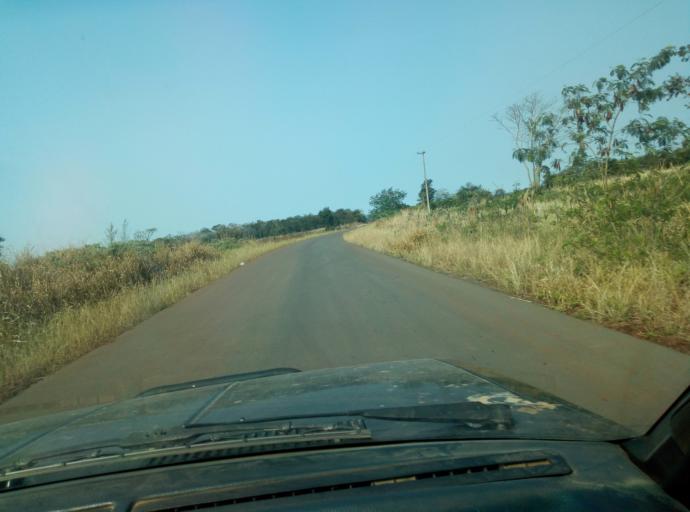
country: PY
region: Caaguazu
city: Carayao
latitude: -25.2315
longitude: -56.2890
